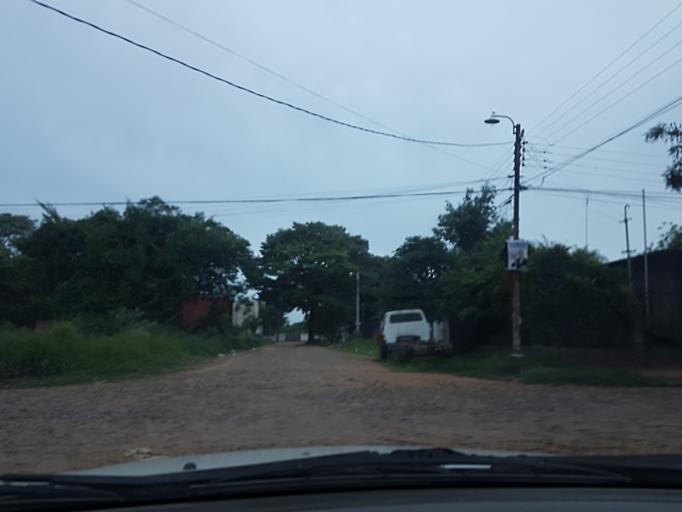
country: PY
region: Central
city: Colonia Mariano Roque Alonso
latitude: -25.2373
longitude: -57.5373
